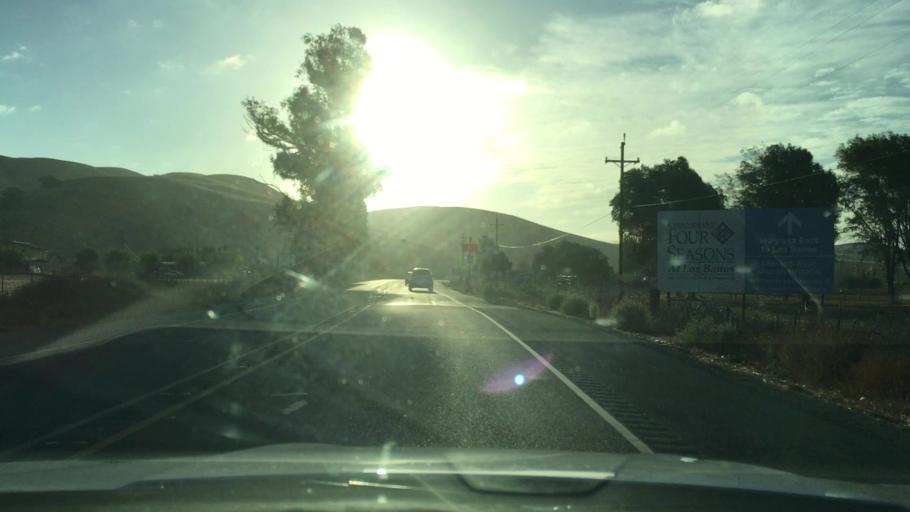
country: US
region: California
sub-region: San Benito County
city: Hollister
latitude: 36.9718
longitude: -121.4221
